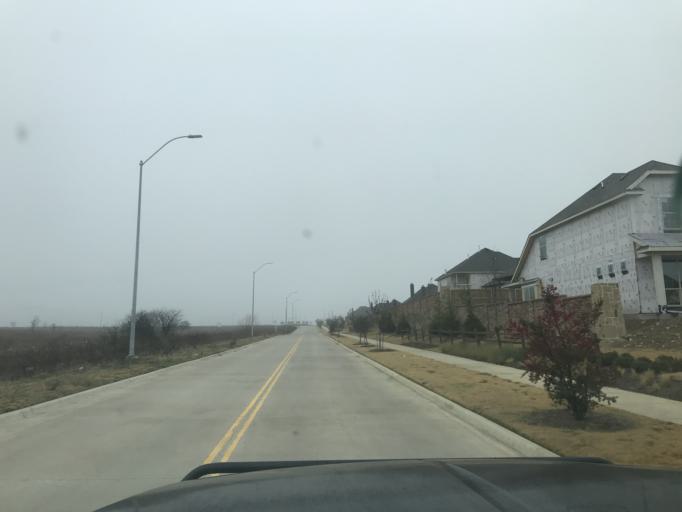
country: US
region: Texas
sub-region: Tarrant County
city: Crowley
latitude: 32.6104
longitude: -97.4178
